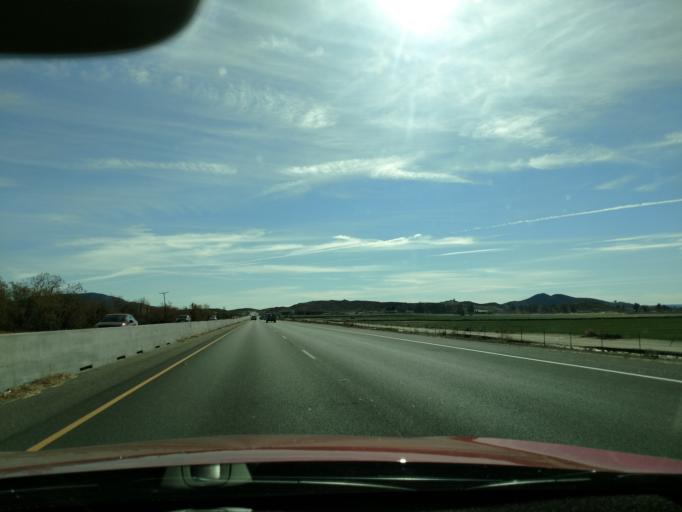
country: US
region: California
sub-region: Riverside County
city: Winchester
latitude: 33.6682
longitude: -117.0849
